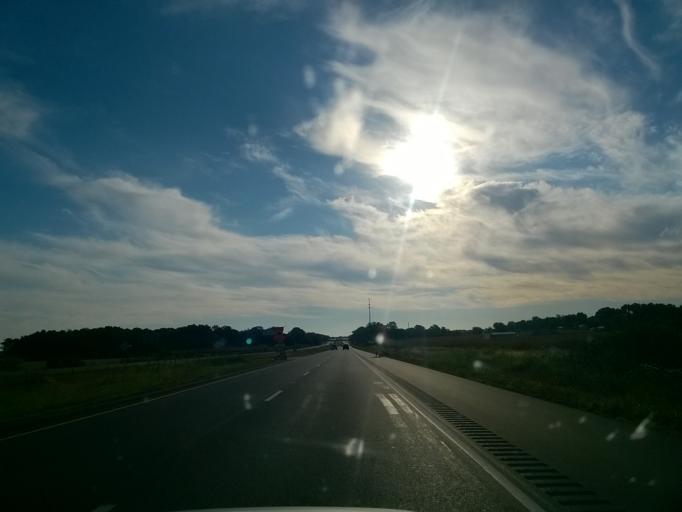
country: US
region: Indiana
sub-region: Gibson County
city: Haubstadt
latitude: 38.1696
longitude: -87.4556
